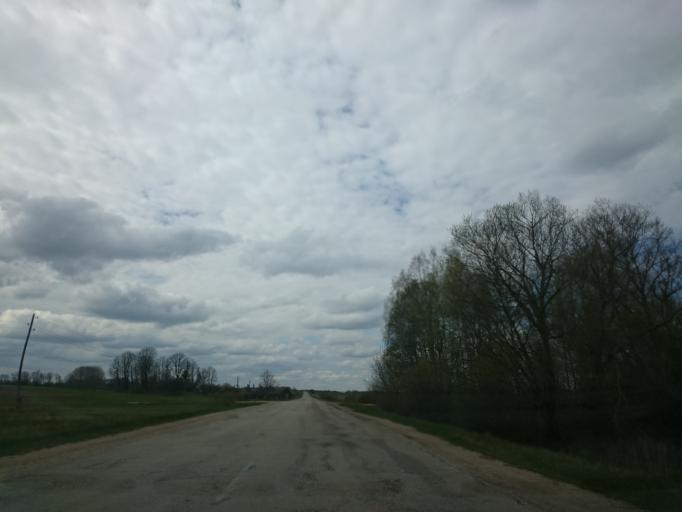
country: LV
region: Jaunpils
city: Jaunpils
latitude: 56.9091
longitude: 22.9606
